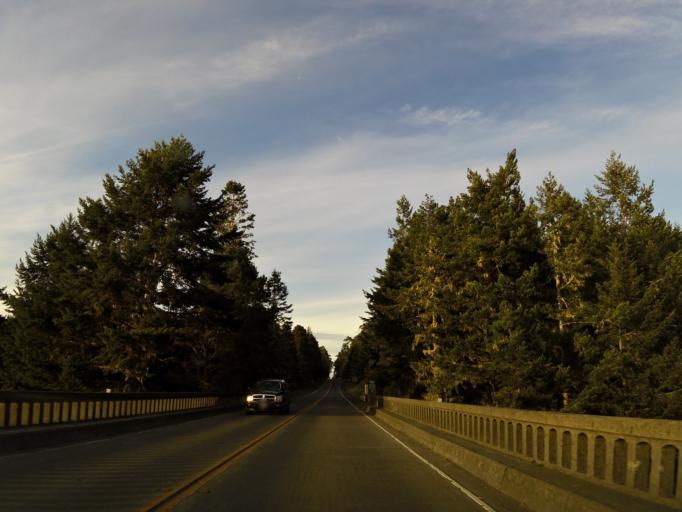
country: US
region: California
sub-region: Mendocino County
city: Fort Bragg
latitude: 39.3293
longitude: -123.8046
